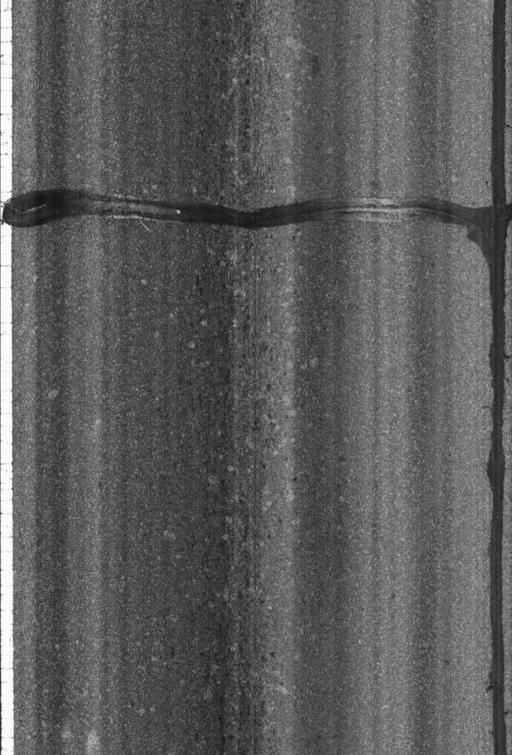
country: US
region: Maryland
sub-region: Prince George's County
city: Hillcrest Heights
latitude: 38.8491
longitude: -76.9661
